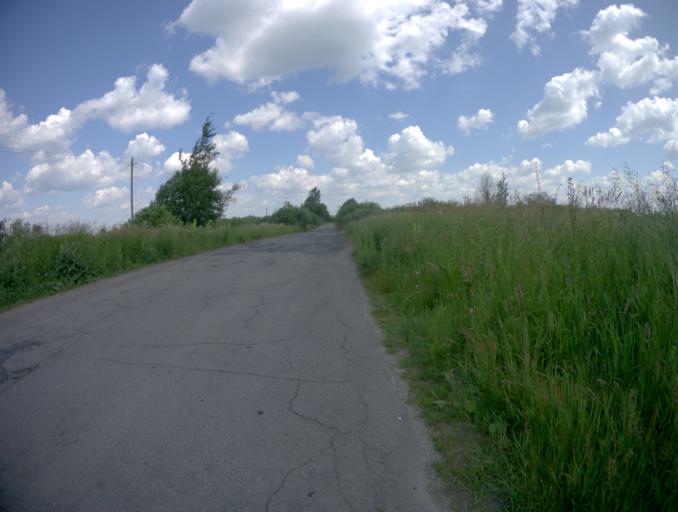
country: RU
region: Vladimir
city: Vyazniki
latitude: 56.3116
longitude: 42.1238
